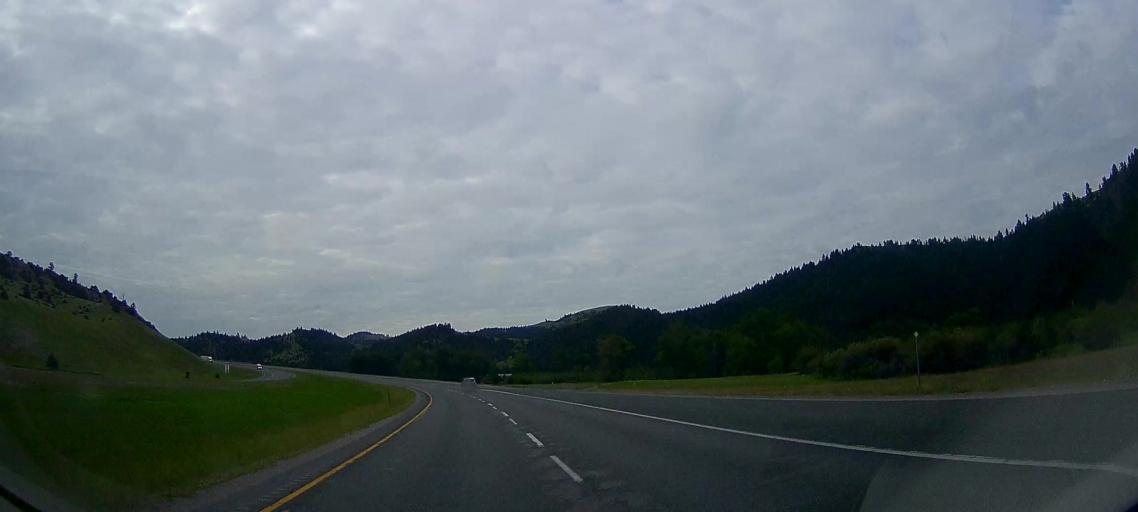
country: US
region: Montana
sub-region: Powell County
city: Deer Lodge
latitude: 46.5605
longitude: -112.8875
